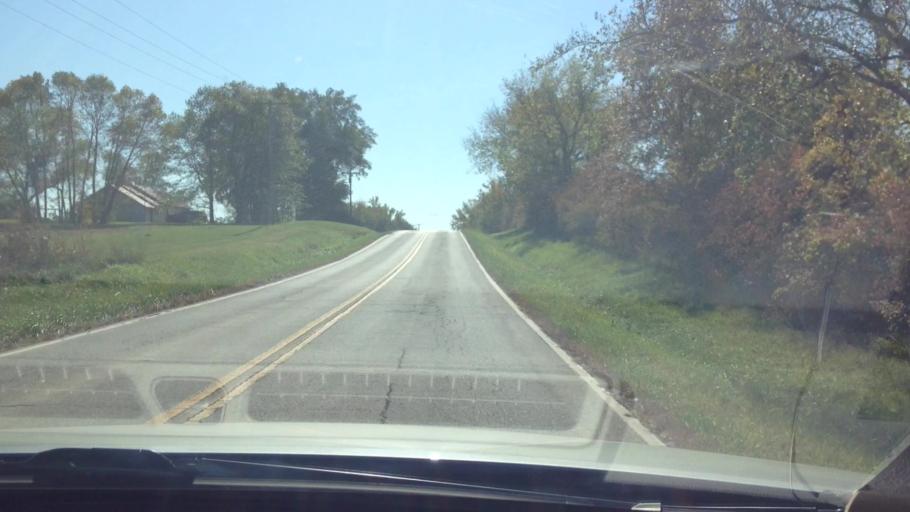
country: US
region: Missouri
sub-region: Clay County
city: Smithville
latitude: 39.3330
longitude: -94.6487
